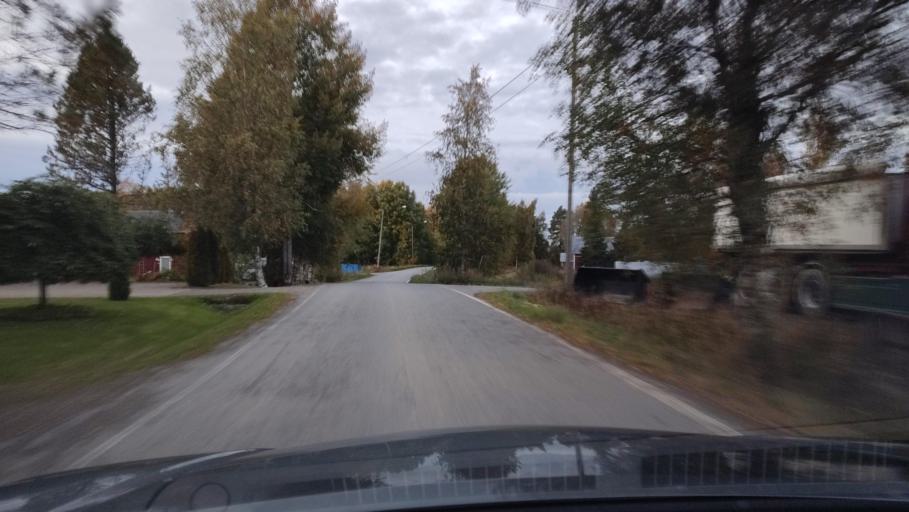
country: FI
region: Ostrobothnia
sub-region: Sydosterbotten
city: Kristinestad
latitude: 62.2653
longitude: 21.5095
